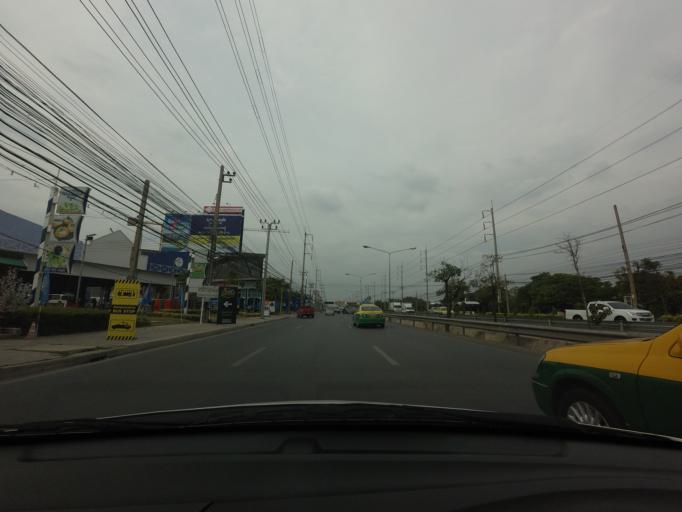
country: TH
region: Samut Prakan
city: Samut Prakan
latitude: 13.5429
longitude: 100.6195
